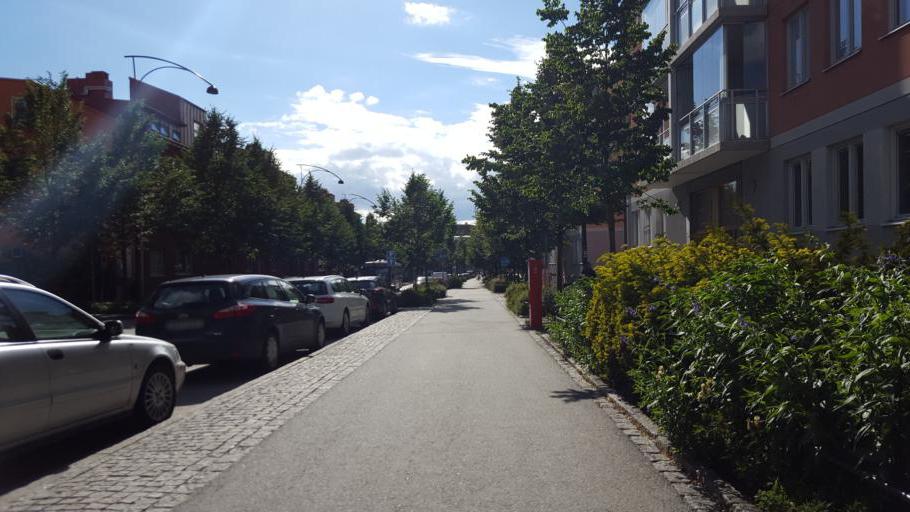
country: SE
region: Stockholm
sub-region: Upplands Vasby Kommun
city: Upplands Vaesby
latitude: 59.5208
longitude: 17.9090
